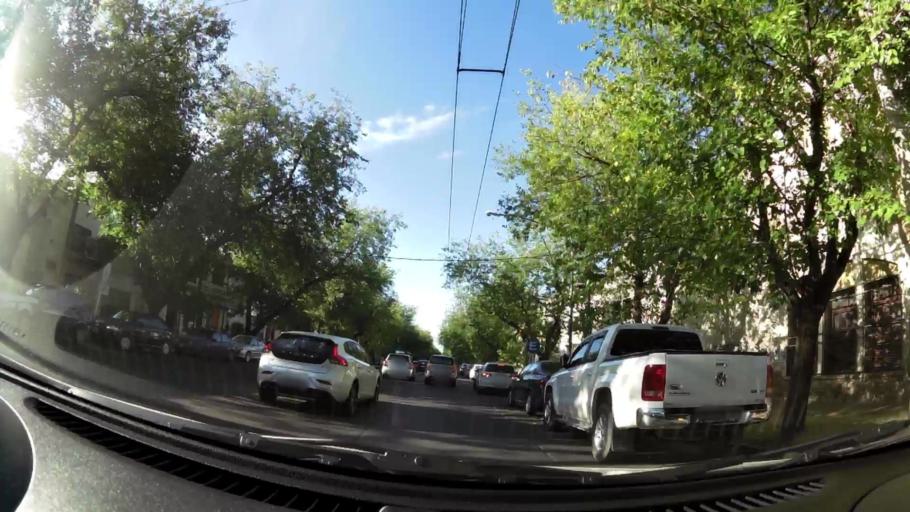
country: AR
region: Mendoza
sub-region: Departamento de Godoy Cruz
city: Godoy Cruz
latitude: -32.9101
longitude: -68.8444
